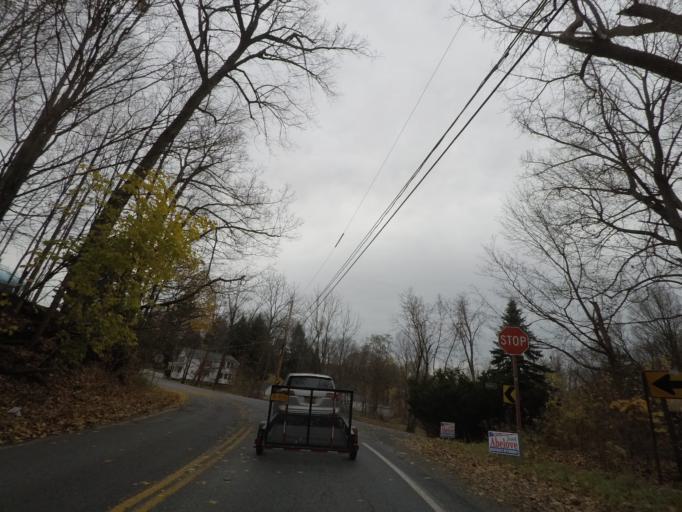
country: US
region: New York
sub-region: Rensselaer County
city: Troy
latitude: 42.7333
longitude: -73.6555
